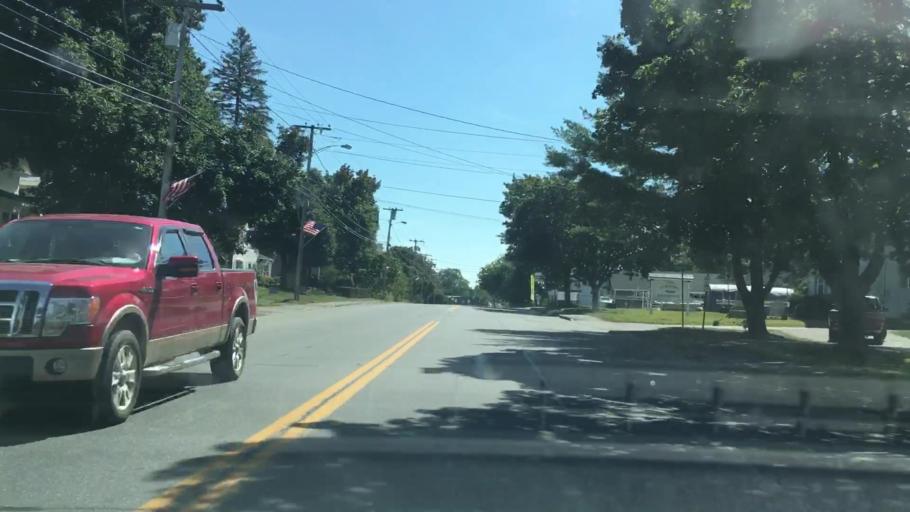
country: US
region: Maine
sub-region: Piscataquis County
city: Milo
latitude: 45.2556
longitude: -68.9869
